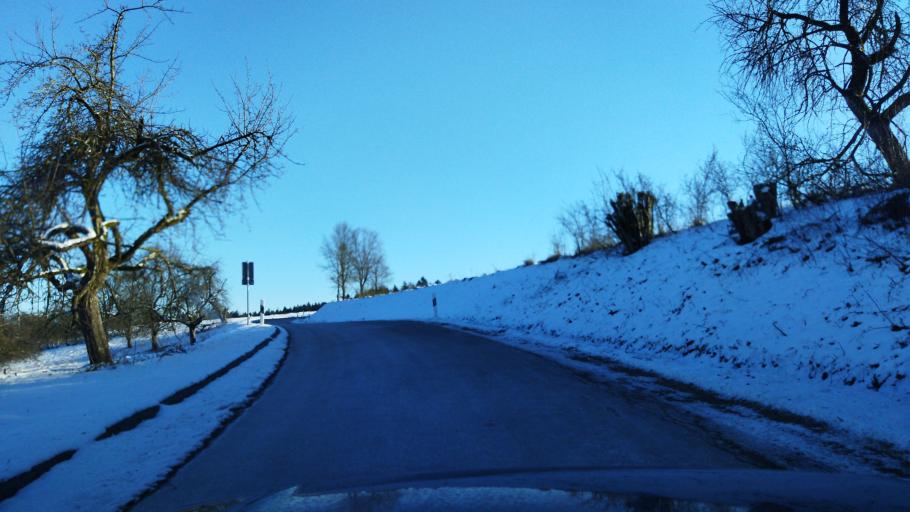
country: DE
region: Baden-Wuerttemberg
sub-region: Regierungsbezirk Stuttgart
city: Gerabronn
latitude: 48.9836
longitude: 9.9176
